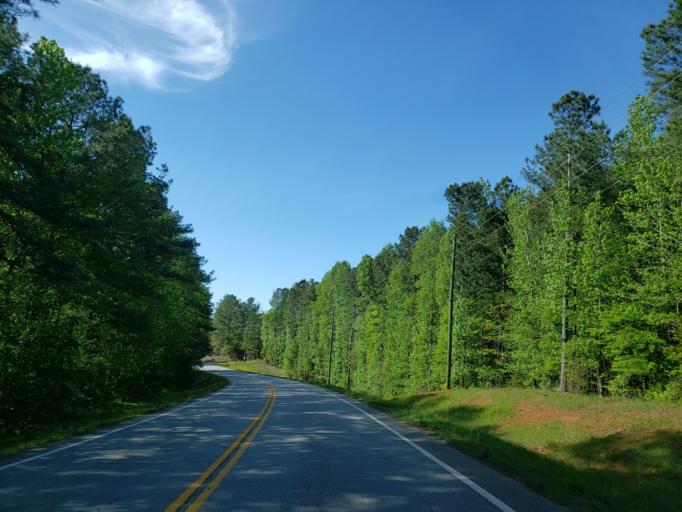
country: US
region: Georgia
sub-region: Haralson County
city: Tallapoosa
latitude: 33.6954
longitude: -85.2627
